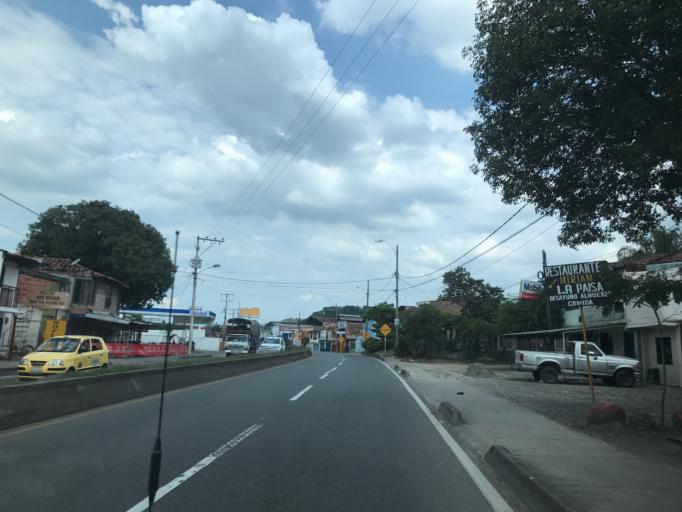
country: CO
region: Valle del Cauca
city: Cartago
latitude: 4.7510
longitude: -75.9007
